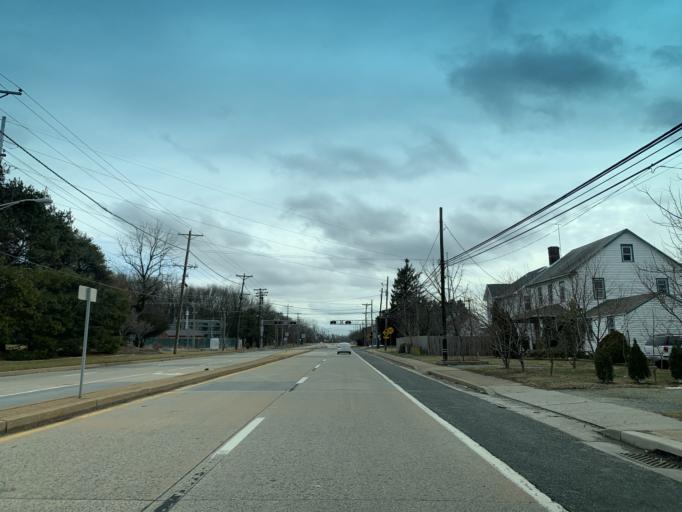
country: US
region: Delaware
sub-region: New Castle County
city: New Castle
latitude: 39.6732
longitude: -75.5613
